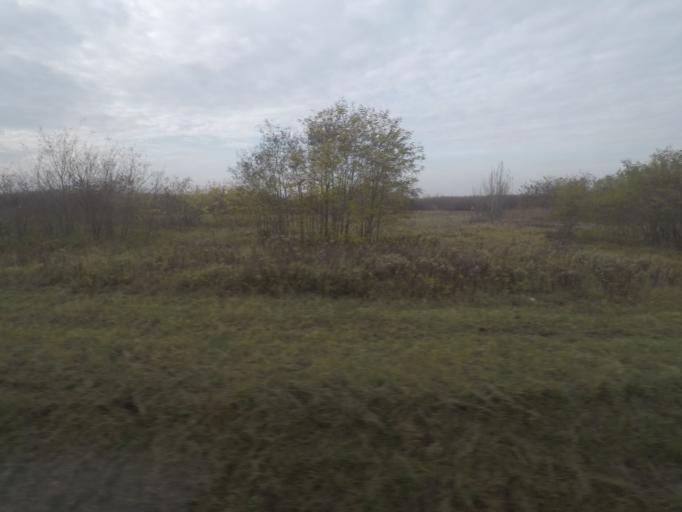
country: PL
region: Subcarpathian Voivodeship
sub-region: Powiat przemyski
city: Medyka
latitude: 49.7906
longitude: 22.8851
